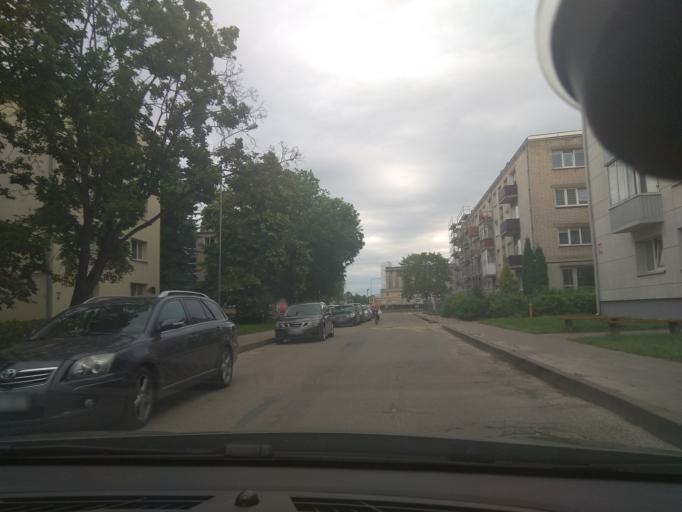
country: LT
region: Marijampoles apskritis
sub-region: Marijampole Municipality
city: Marijampole
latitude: 54.5635
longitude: 23.3605
